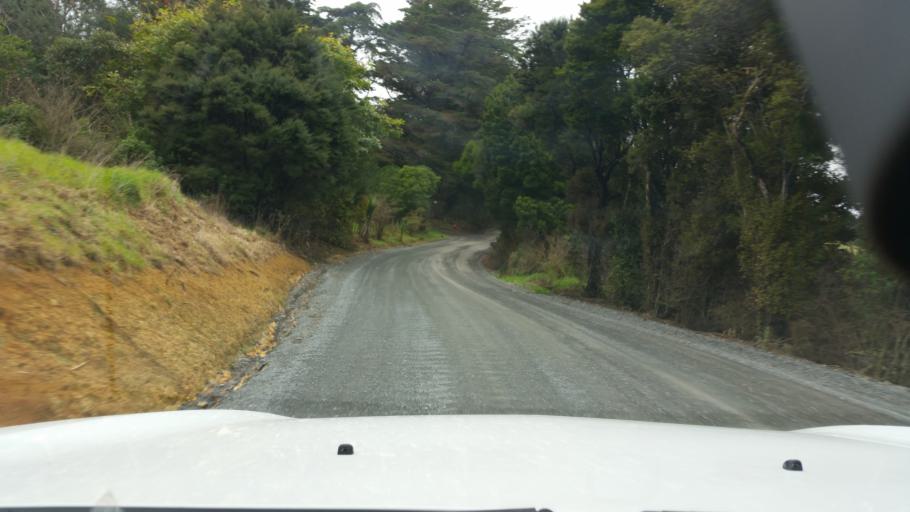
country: NZ
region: Northland
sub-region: Whangarei
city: Whangarei
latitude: -35.7326
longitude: 174.4227
